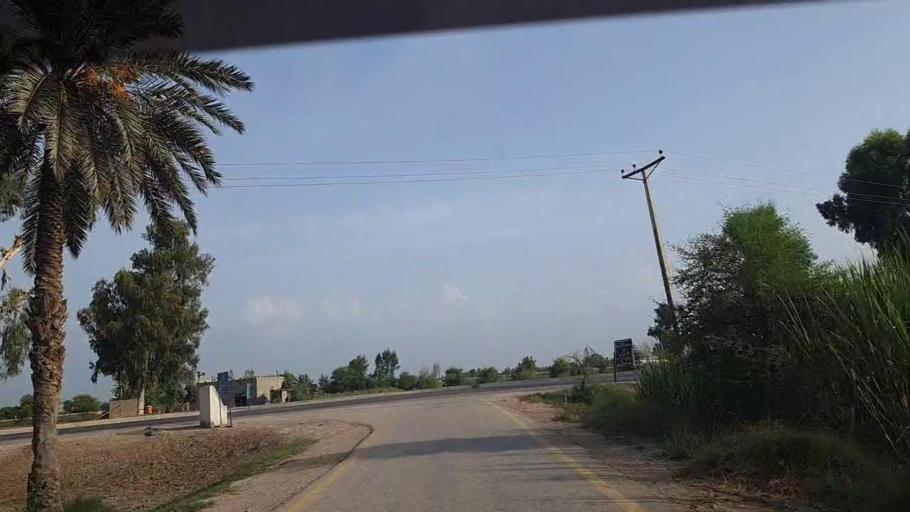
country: PK
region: Sindh
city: Adilpur
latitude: 27.9627
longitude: 69.2564
